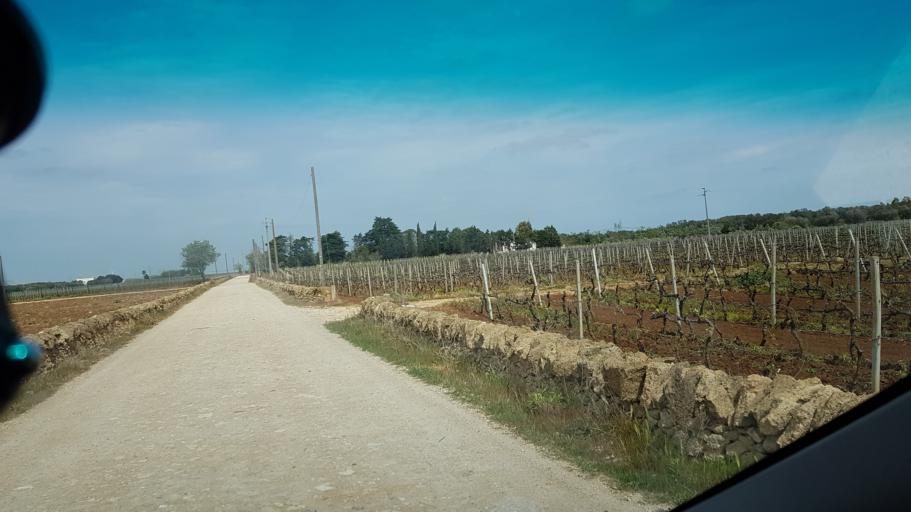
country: IT
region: Apulia
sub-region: Provincia di Brindisi
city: Mesagne
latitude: 40.5960
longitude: 17.8568
